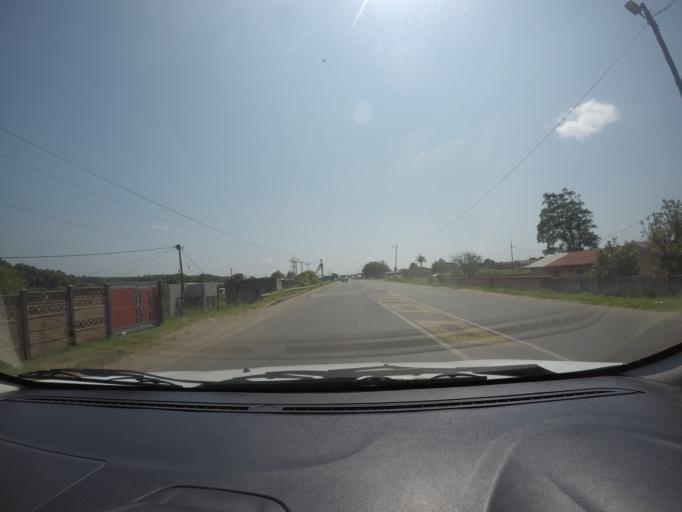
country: ZA
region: KwaZulu-Natal
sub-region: uThungulu District Municipality
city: eSikhawini
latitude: -28.8612
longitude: 31.9161
